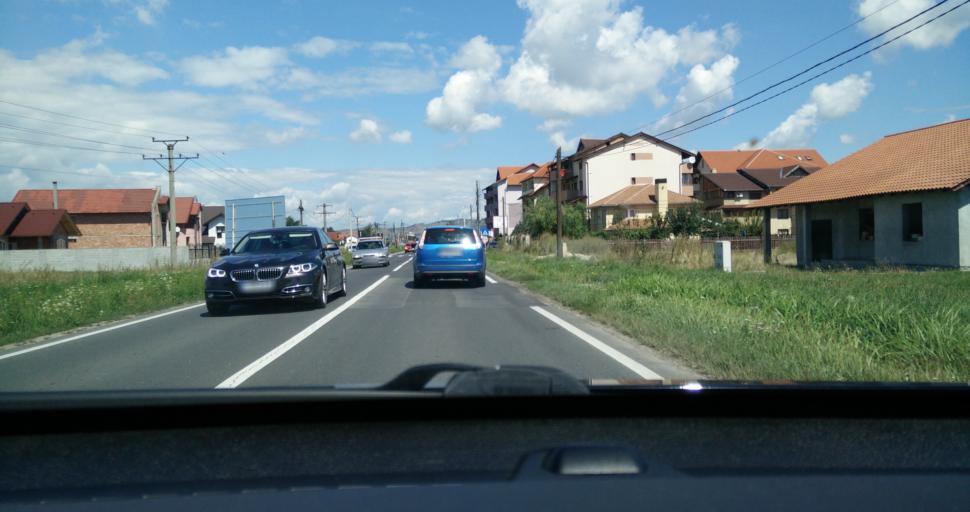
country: RO
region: Alba
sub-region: Municipiul Sebes
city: Petresti
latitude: 45.9364
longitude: 23.5621
